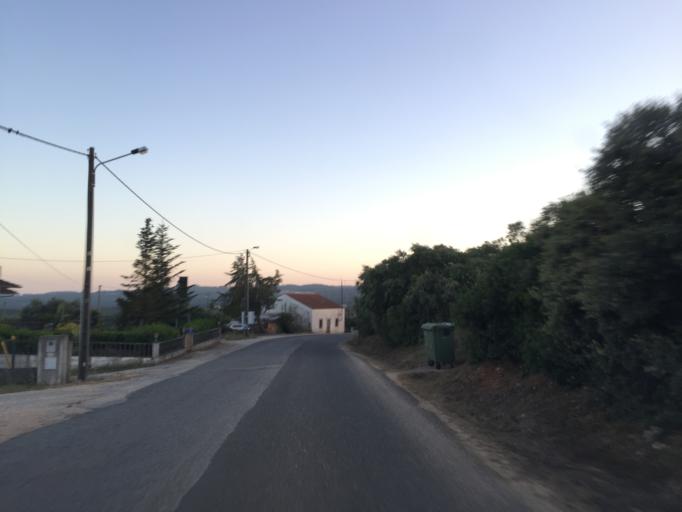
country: PT
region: Santarem
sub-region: Ourem
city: Fatima
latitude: 39.6204
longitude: -8.6480
